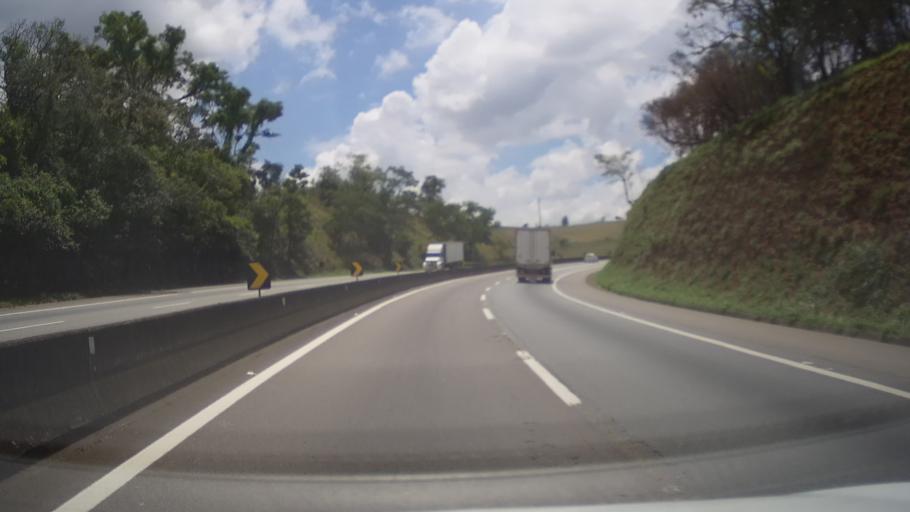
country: BR
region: Minas Gerais
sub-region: Tres Coracoes
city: Tres Coracoes
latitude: -21.6990
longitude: -45.3671
